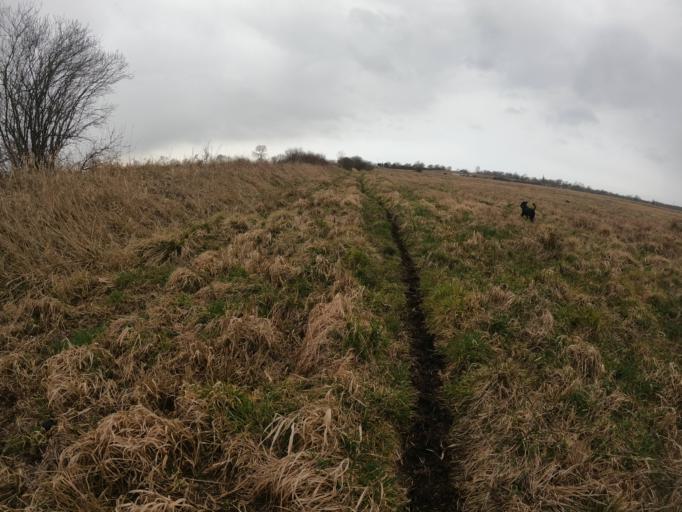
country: PL
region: West Pomeranian Voivodeship
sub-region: Powiat gryficki
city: Trzebiatow
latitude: 54.0769
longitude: 15.2269
